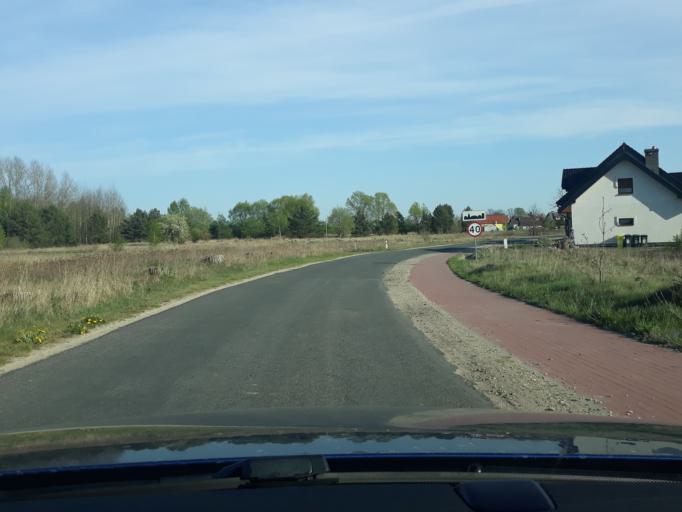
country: PL
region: Pomeranian Voivodeship
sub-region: Powiat czluchowski
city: Przechlewo
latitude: 53.8314
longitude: 17.3761
